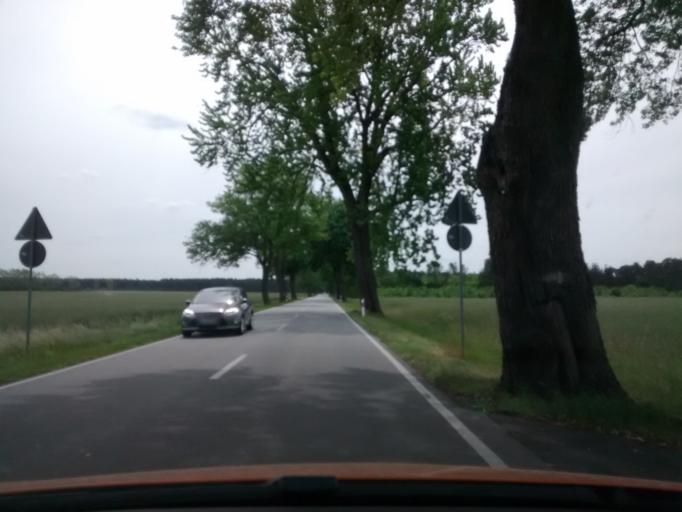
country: DE
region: Brandenburg
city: Juterbog
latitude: 51.8974
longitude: 13.1405
